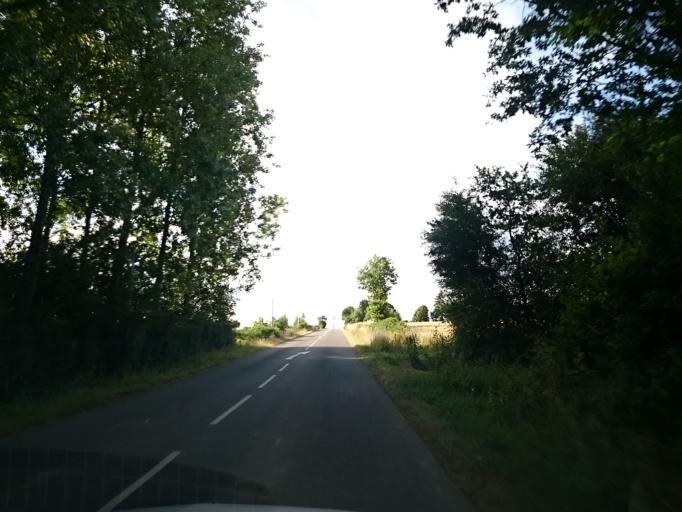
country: FR
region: Brittany
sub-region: Departement d'Ille-et-Vilaine
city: Chanteloup
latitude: 47.9148
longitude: -1.6172
